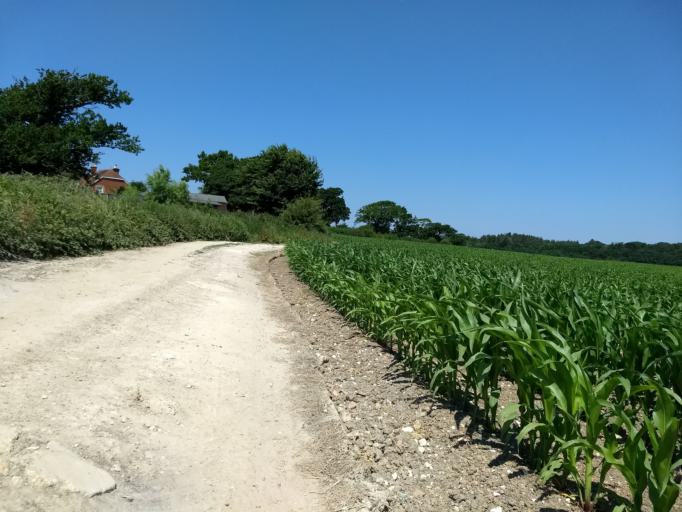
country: GB
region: England
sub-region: Isle of Wight
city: Newport
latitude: 50.7003
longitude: -1.3286
